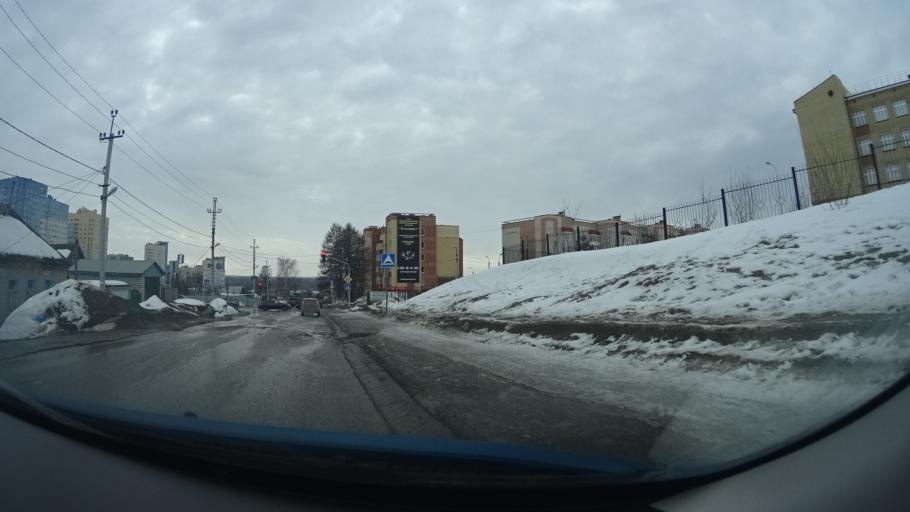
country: RU
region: Bashkortostan
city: Ufa
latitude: 54.6939
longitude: 55.9884
